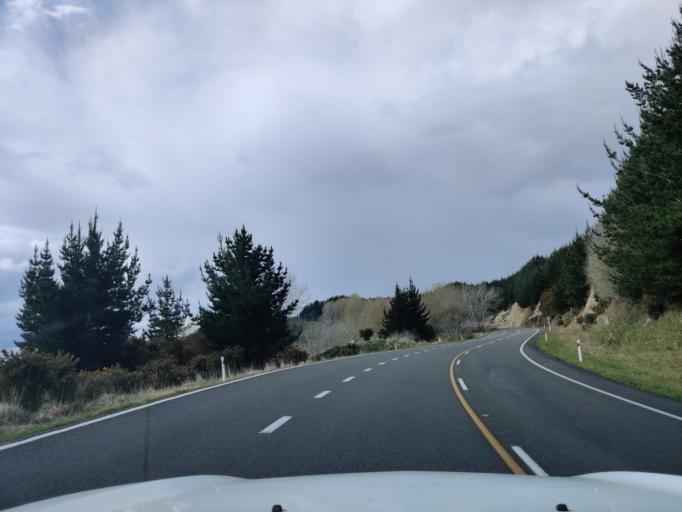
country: NZ
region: Manawatu-Wanganui
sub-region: Wanganui District
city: Wanganui
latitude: -39.8014
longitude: 175.1926
